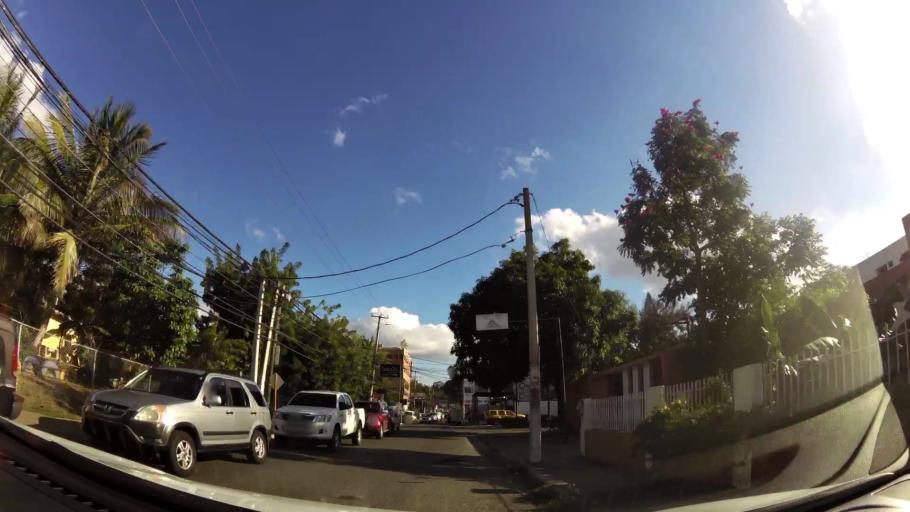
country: DO
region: Santiago
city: Santiago de los Caballeros
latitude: 19.4634
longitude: -70.6889
